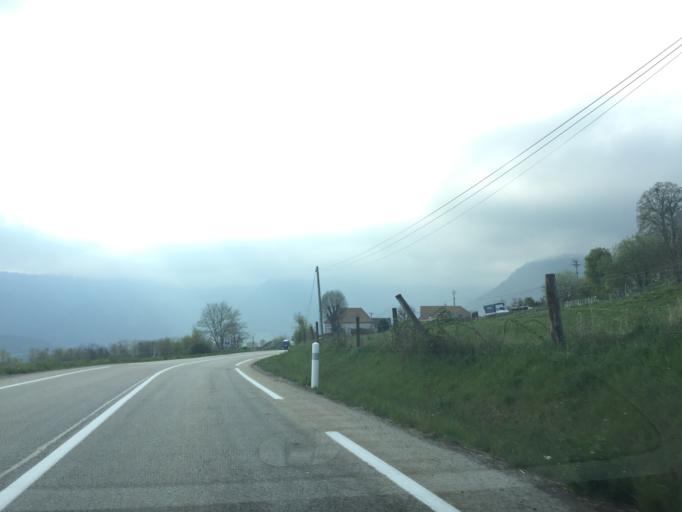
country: FR
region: Rhone-Alpes
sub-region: Departement de l'Isere
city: Mens
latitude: 44.7730
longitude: 5.6600
